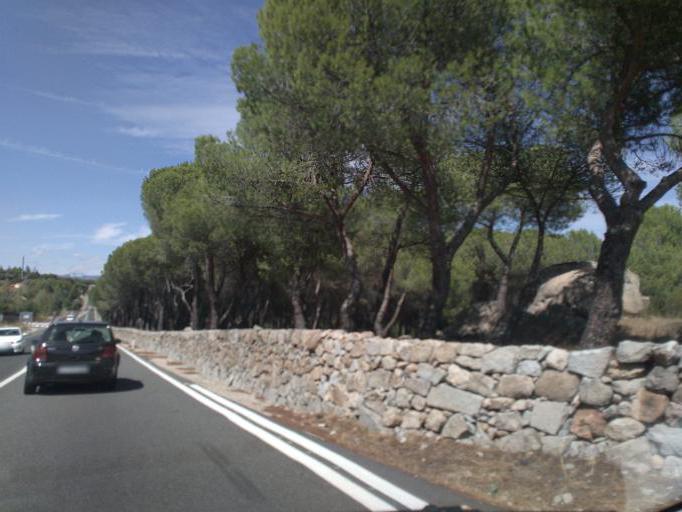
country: ES
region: Madrid
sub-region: Provincia de Madrid
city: Torrelodones
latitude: 40.5560
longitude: -3.9626
